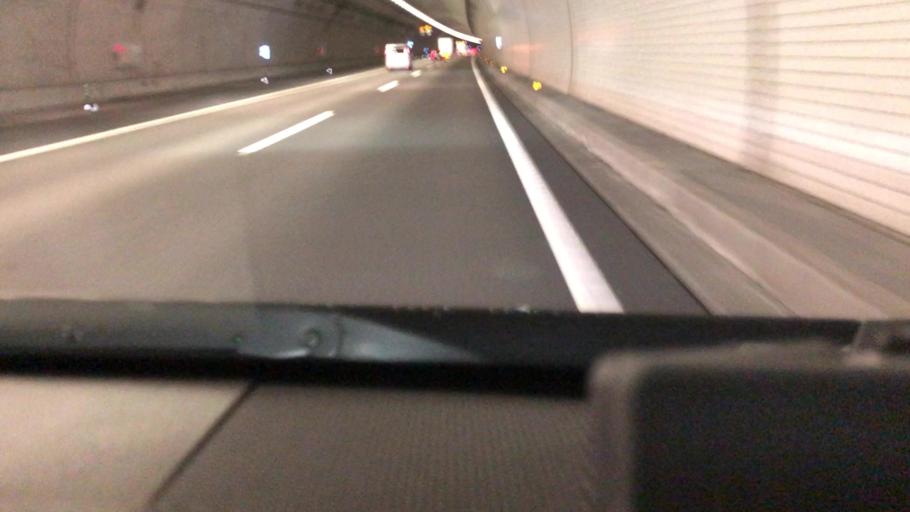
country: JP
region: Shizuoka
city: Fujieda
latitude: 34.9425
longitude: 138.2795
